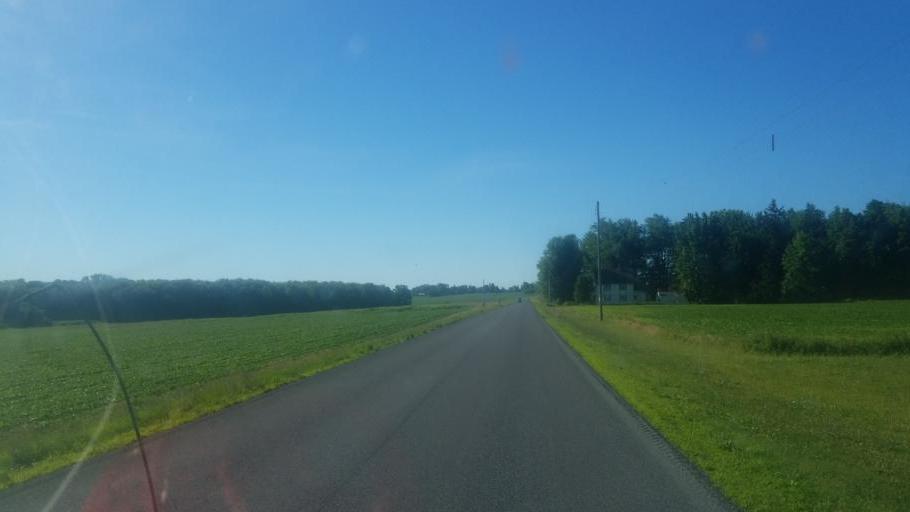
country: US
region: New York
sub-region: Ontario County
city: Phelps
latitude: 42.8962
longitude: -77.0534
